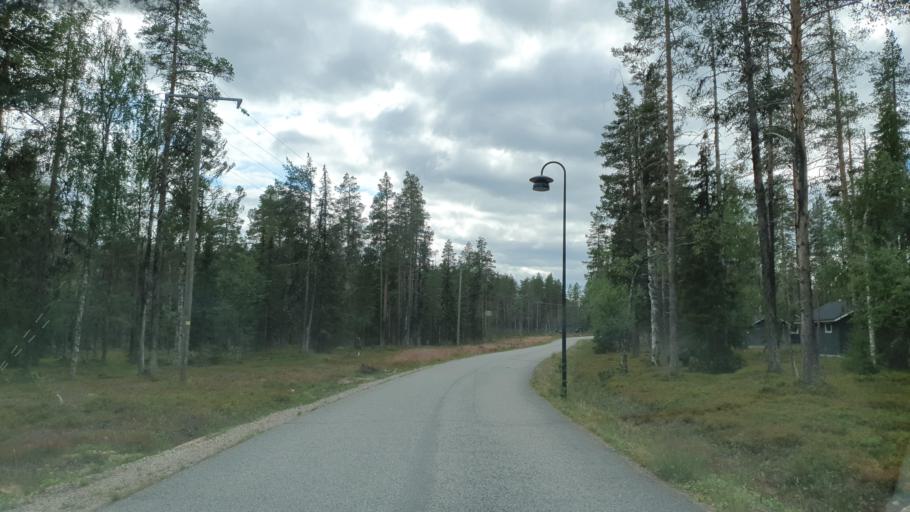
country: FI
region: Lapland
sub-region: Tunturi-Lappi
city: Kolari
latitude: 67.5486
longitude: 24.2771
